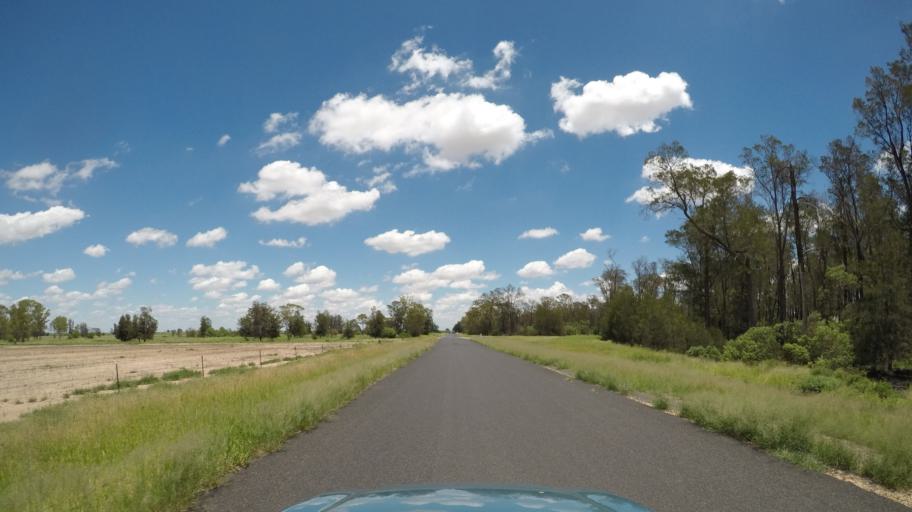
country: AU
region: Queensland
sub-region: Goondiwindi
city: Goondiwindi
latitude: -28.1559
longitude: 150.3748
